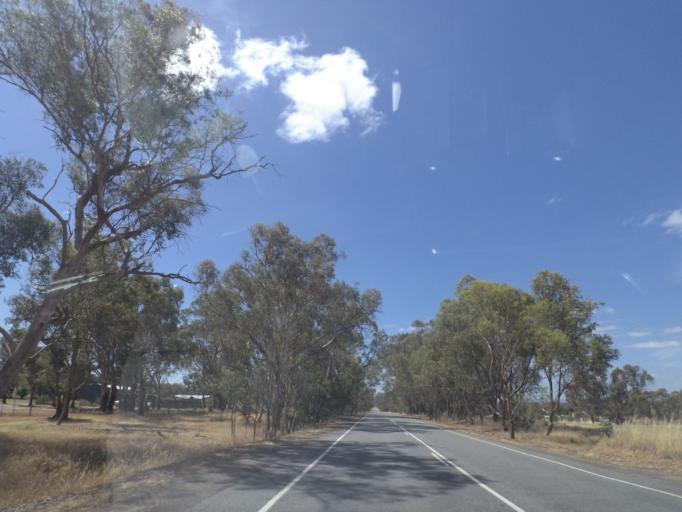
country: AU
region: Victoria
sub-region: Wangaratta
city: Wangaratta
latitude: -36.4492
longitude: 146.2392
